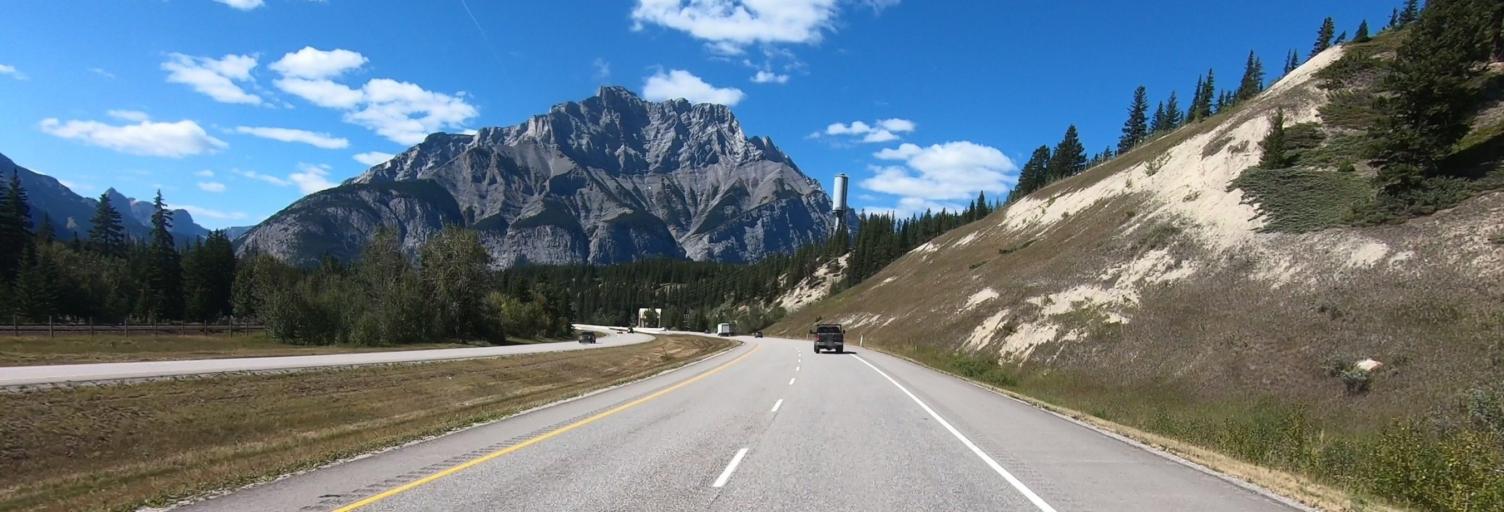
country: CA
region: Alberta
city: Banff
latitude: 51.1974
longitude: -115.4972
